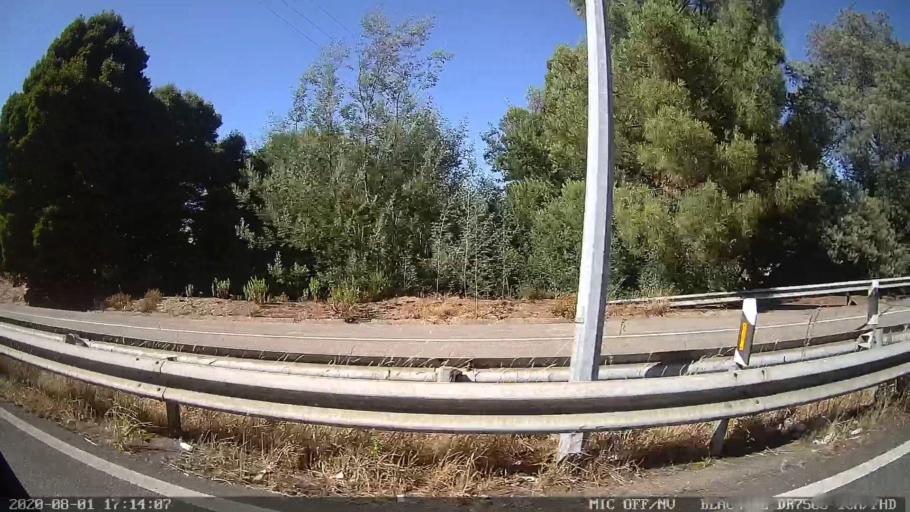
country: PT
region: Porto
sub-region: Santo Tirso
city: Santo Tirso
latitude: 41.3377
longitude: -8.5022
